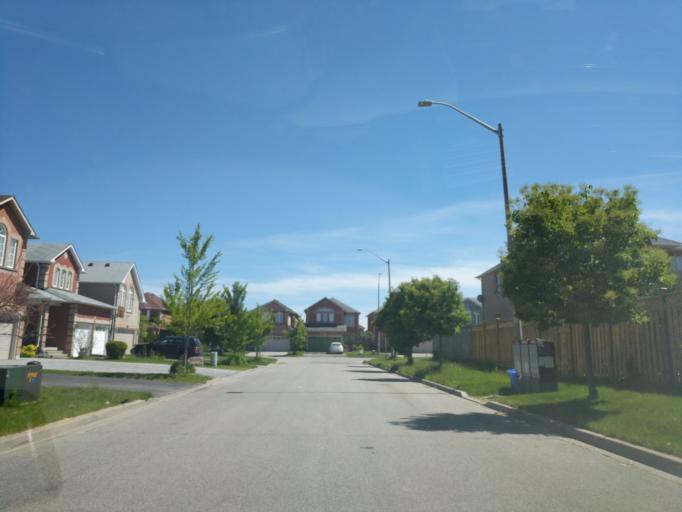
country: CA
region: Ontario
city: Markham
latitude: 43.8509
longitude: -79.2693
